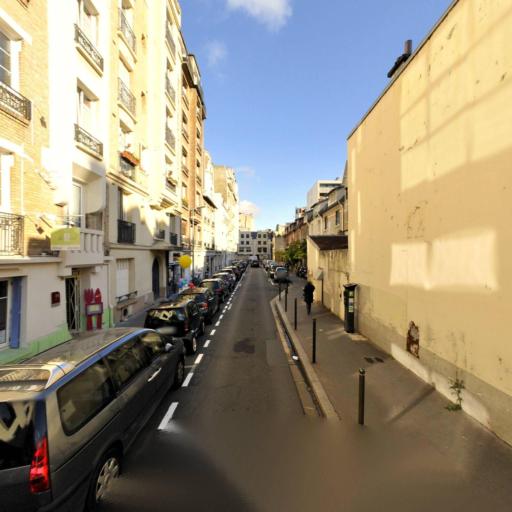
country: FR
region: Ile-de-France
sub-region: Departement des Hauts-de-Seine
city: Boulogne-Billancourt
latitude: 48.8354
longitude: 2.2430
